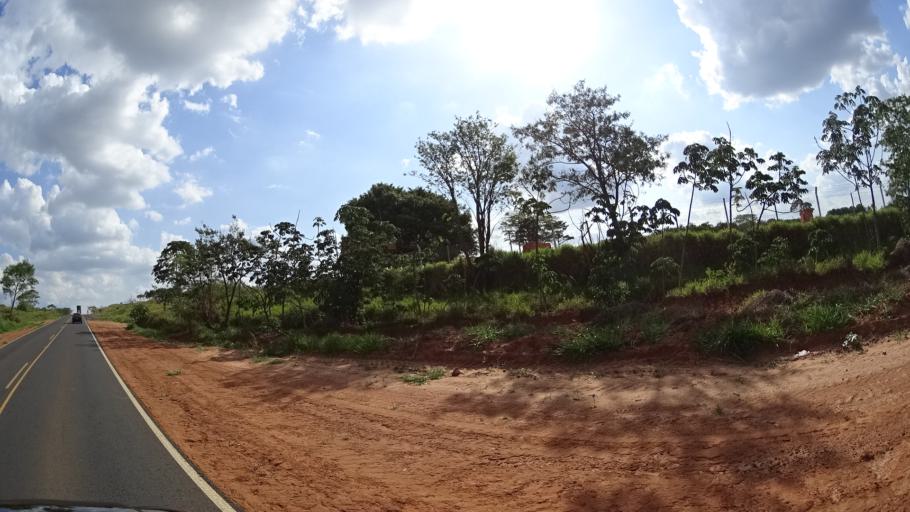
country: BR
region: Sao Paulo
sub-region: Urupes
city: Urupes
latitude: -21.1588
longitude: -49.2858
